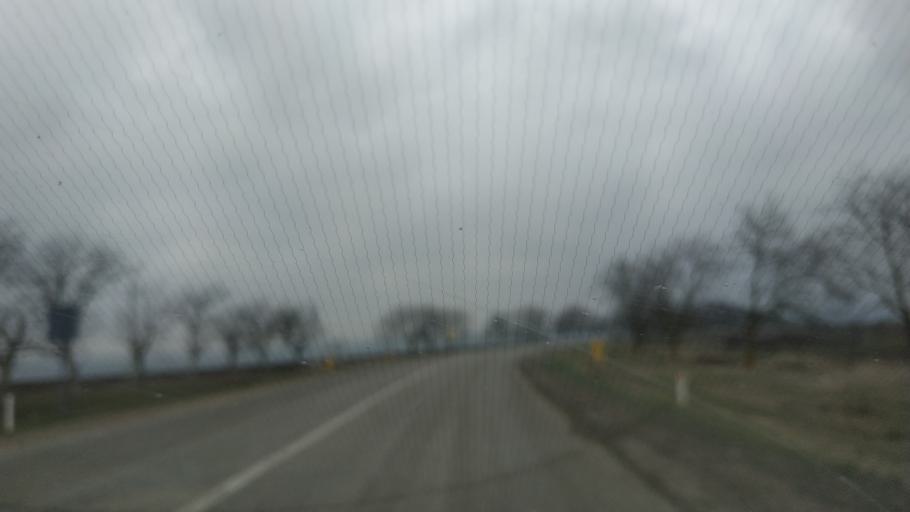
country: MD
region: Gagauzia
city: Comrat
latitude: 46.2621
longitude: 28.7474
